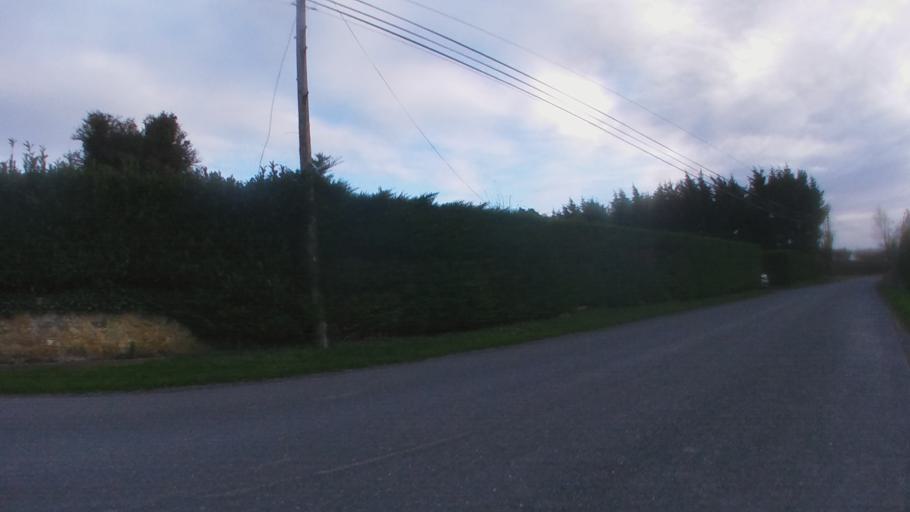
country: IE
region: Leinster
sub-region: Kilkenny
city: Kilkenny
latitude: 52.6832
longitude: -7.1763
